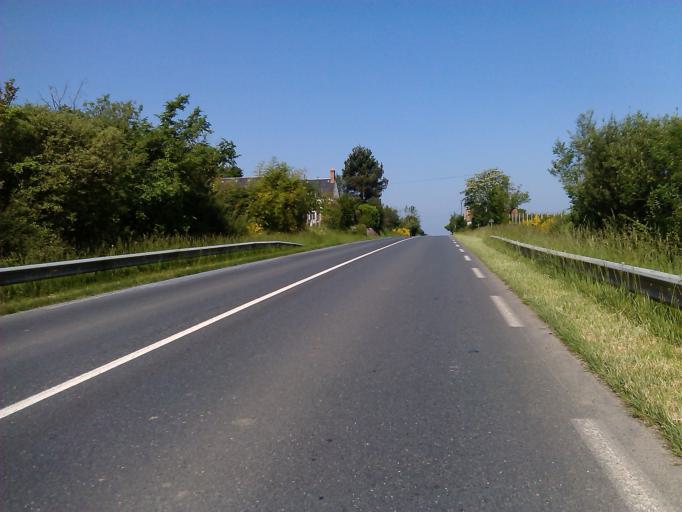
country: FR
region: Centre
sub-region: Departement de l'Indre
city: Cluis
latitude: 46.6094
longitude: 1.7029
